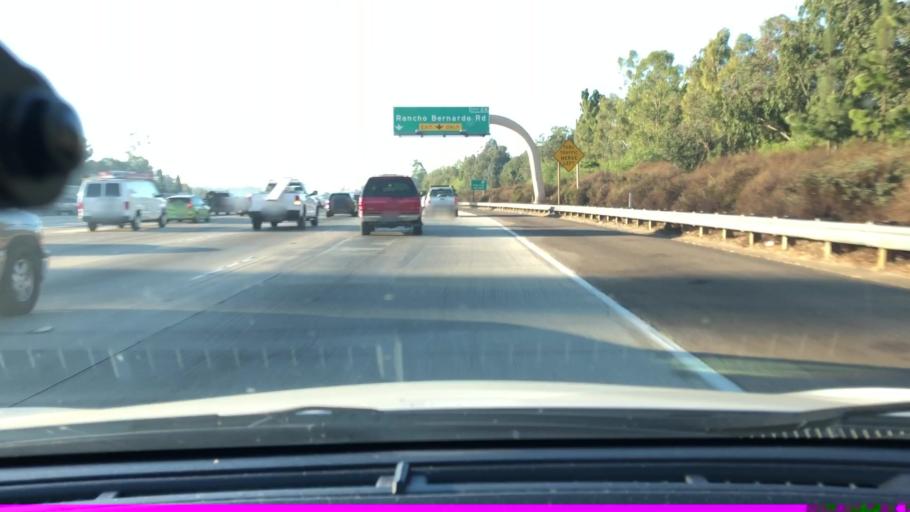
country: US
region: California
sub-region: San Diego County
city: Poway
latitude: 33.0312
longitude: -117.0788
